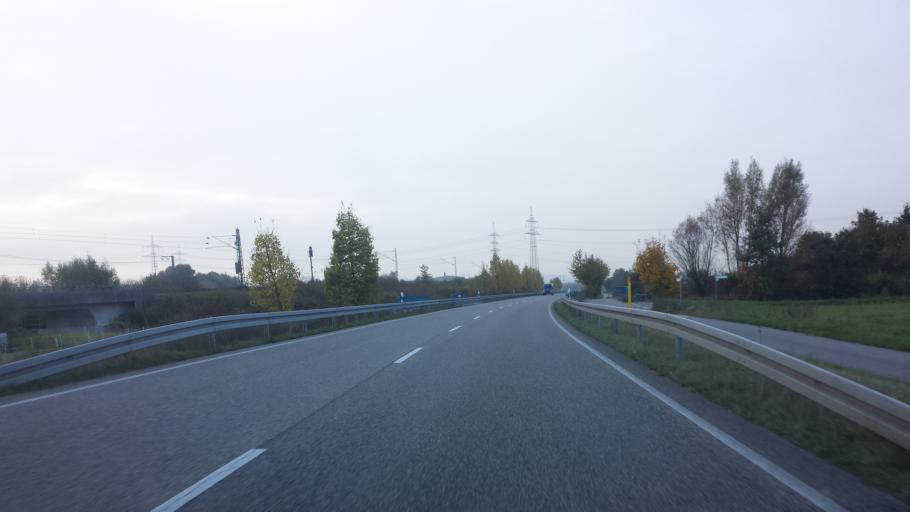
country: DE
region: Baden-Wuerttemberg
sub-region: Karlsruhe Region
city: Ubstadt-Weiher
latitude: 49.1620
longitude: 8.6180
